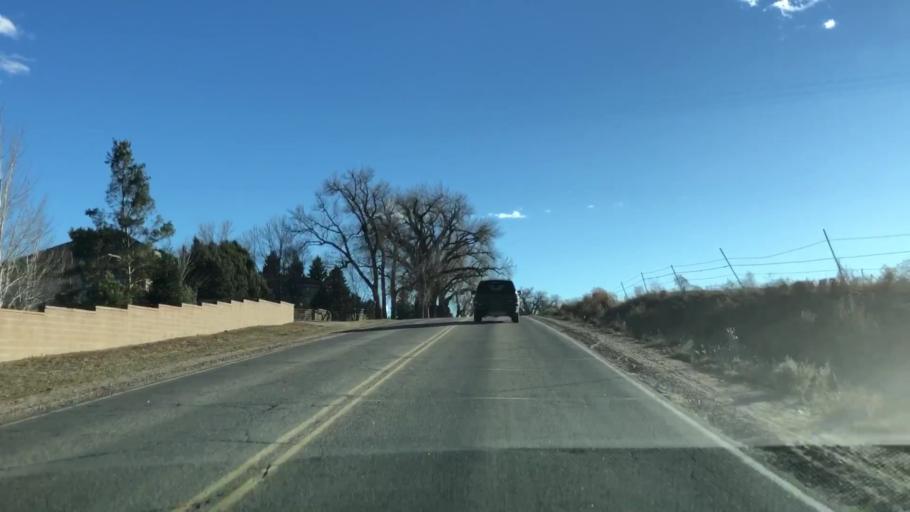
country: US
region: Colorado
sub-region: Weld County
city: Windsor
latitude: 40.4845
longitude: -104.9820
